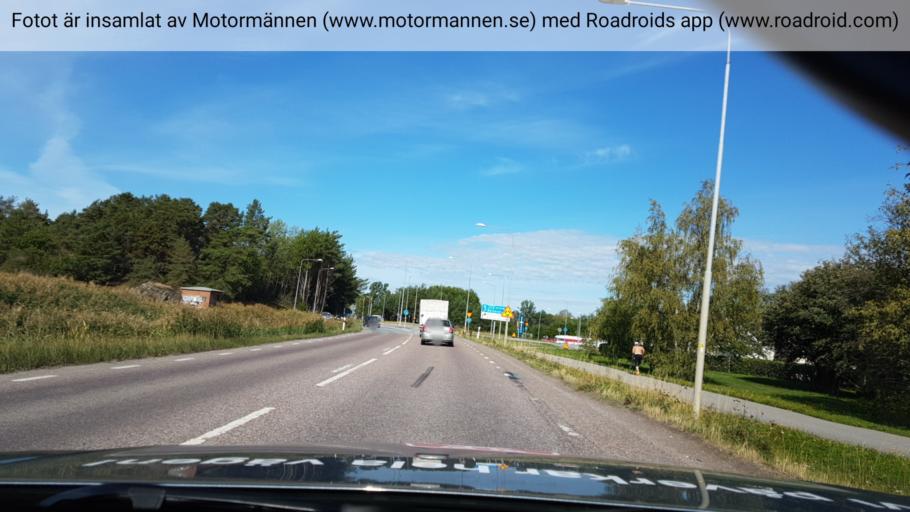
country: SE
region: Uppsala
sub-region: Uppsala Kommun
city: Gamla Uppsala
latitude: 59.8762
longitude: 17.5910
